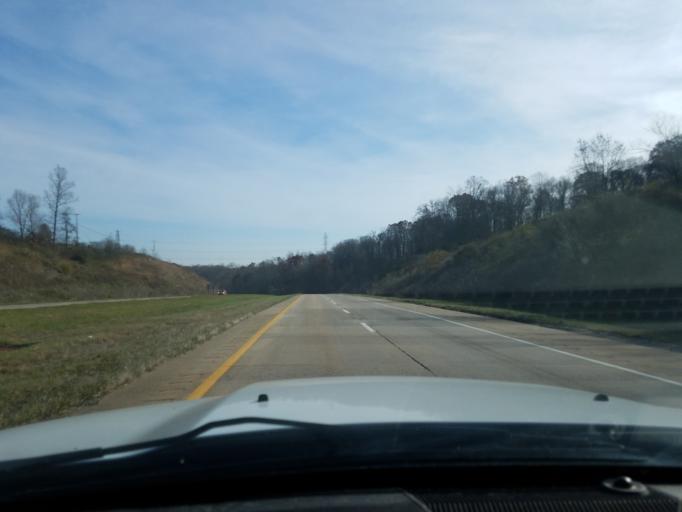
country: US
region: West Virginia
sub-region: Wood County
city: Washington
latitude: 39.2184
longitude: -81.8634
